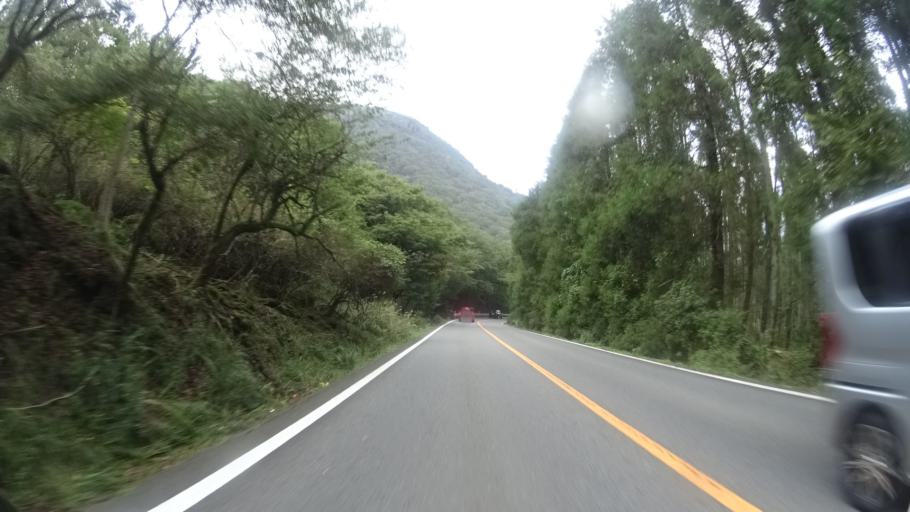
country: JP
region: Oita
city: Beppu
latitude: 33.2693
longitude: 131.4079
